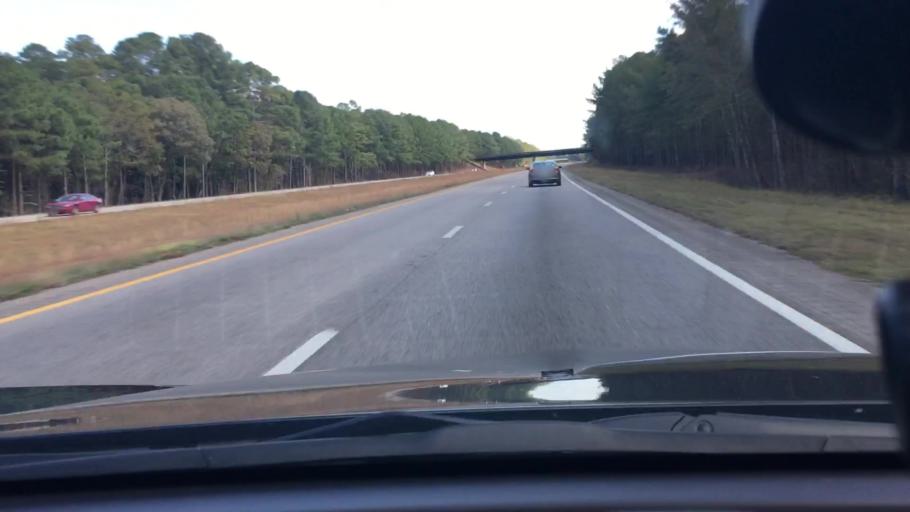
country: US
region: North Carolina
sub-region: Wilson County
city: Lucama
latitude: 35.7833
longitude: -78.0927
